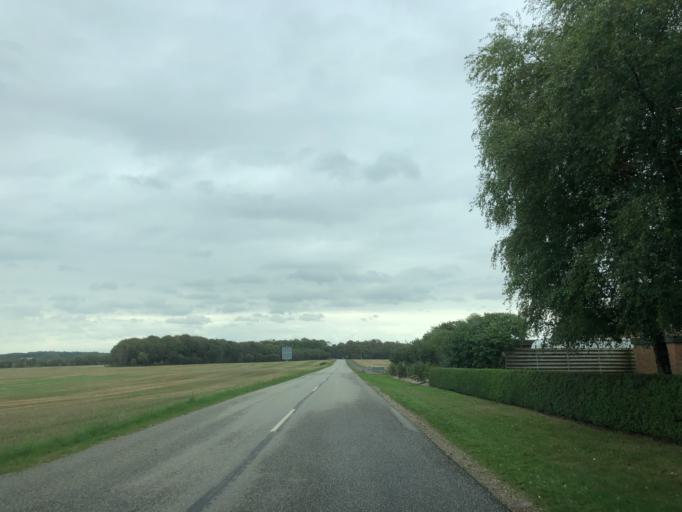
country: DK
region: Central Jutland
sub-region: Herning Kommune
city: Snejbjerg
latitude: 56.1709
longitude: 8.8511
